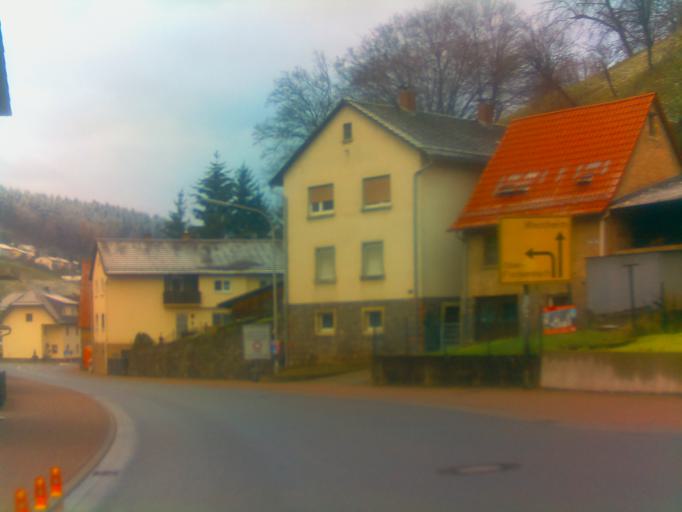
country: DE
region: Hesse
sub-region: Regierungsbezirk Darmstadt
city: Birkenau
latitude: 49.5309
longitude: 8.7342
